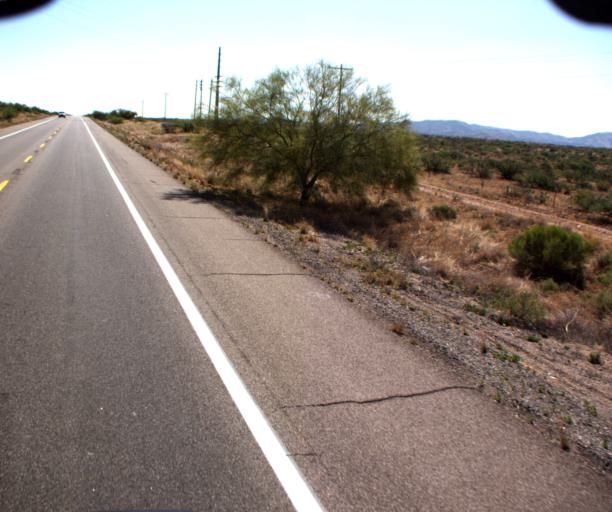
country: US
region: Arizona
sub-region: Pima County
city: Catalina
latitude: 32.5989
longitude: -110.8756
